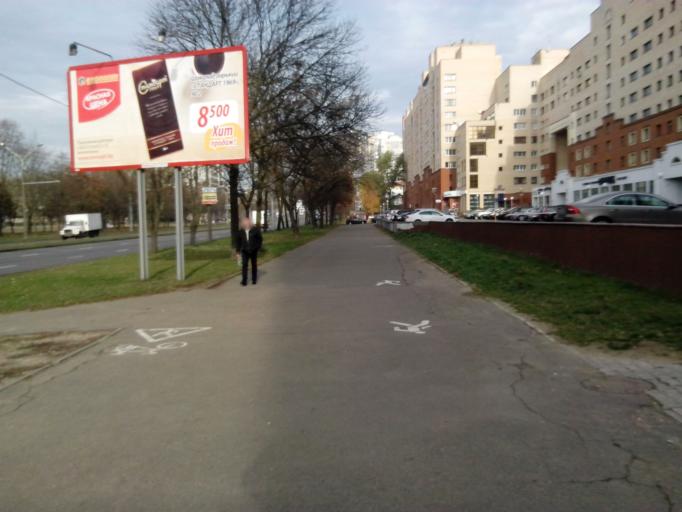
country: BY
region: Minsk
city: Minsk
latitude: 53.9327
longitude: 27.5788
